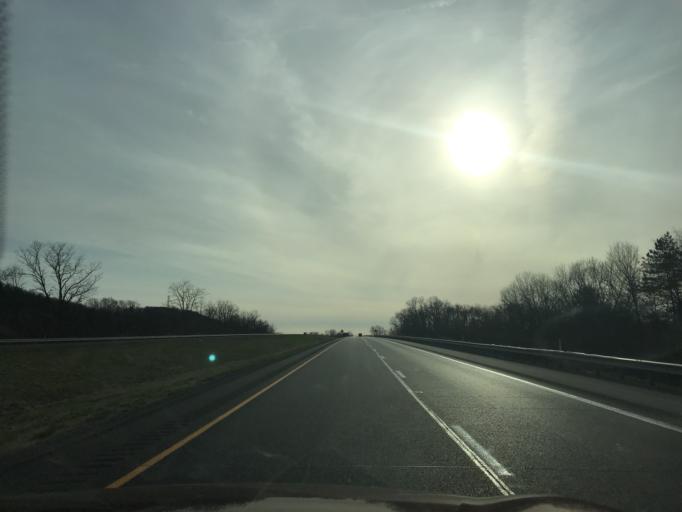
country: US
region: Pennsylvania
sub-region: Lycoming County
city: Muncy
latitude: 41.1889
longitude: -76.7795
